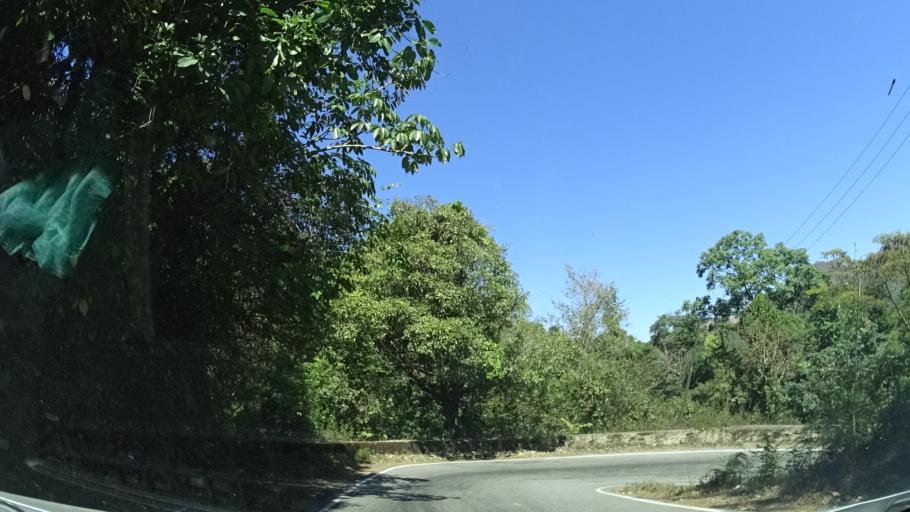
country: IN
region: Karnataka
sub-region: Chikmagalur
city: Sringeri
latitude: 13.1994
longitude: 75.2850
